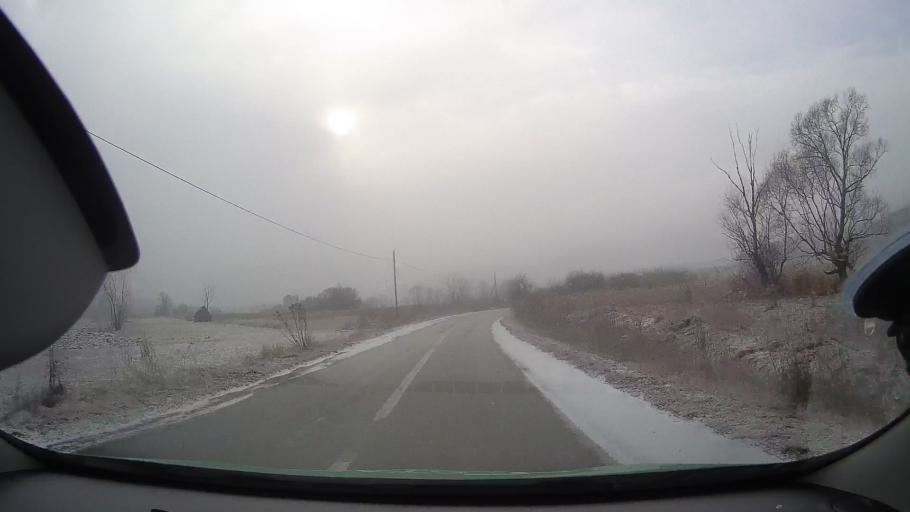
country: RO
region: Alba
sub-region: Comuna Rimetea
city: Rimetea
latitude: 46.4068
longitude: 23.5576
